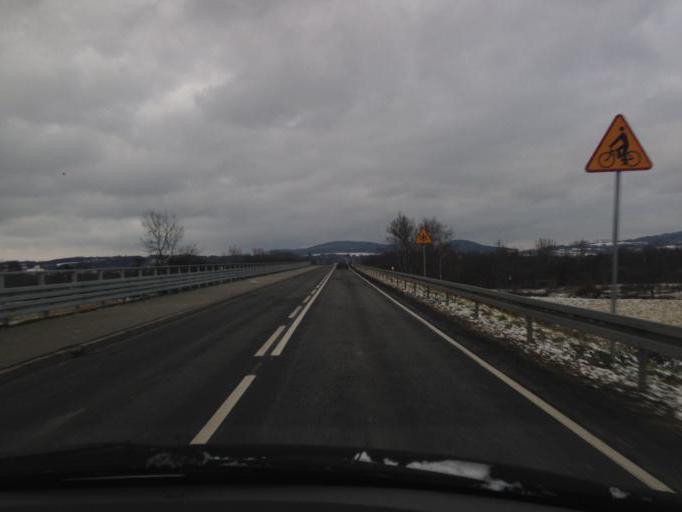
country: PL
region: Lesser Poland Voivodeship
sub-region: Powiat tarnowski
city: Zakliczyn
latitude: 49.8682
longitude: 20.8116
